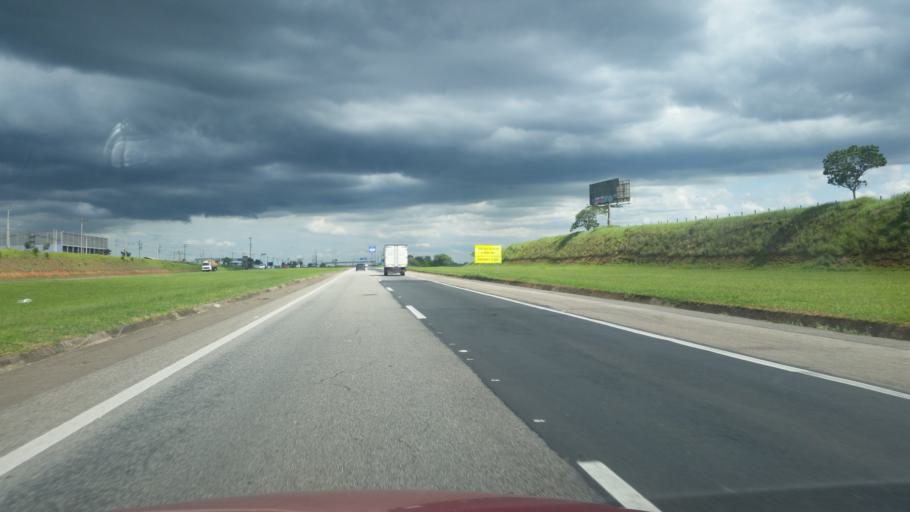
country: BR
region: Sao Paulo
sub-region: Boituva
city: Boituva
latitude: -23.3076
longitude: -47.6533
